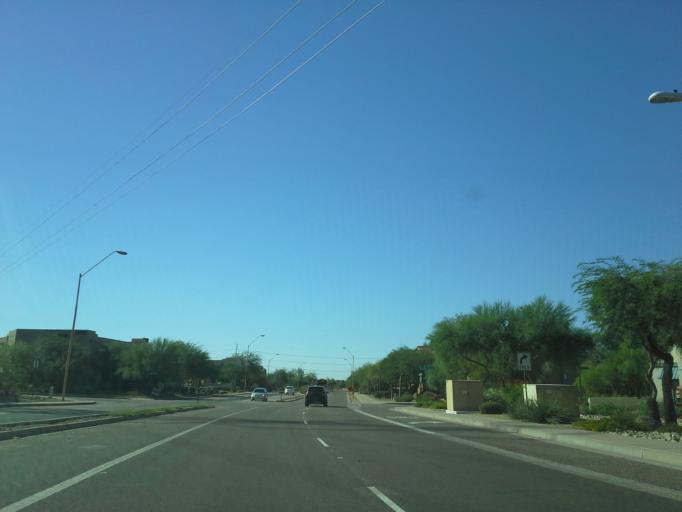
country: US
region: Arizona
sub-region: Maricopa County
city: Scottsdale
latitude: 33.5871
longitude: -111.8352
